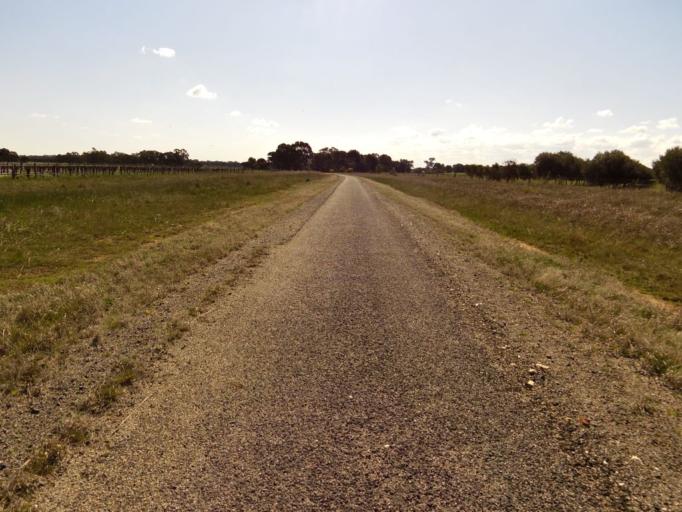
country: AU
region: New South Wales
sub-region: Corowa Shire
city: Corowa
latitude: -36.0400
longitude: 146.4537
